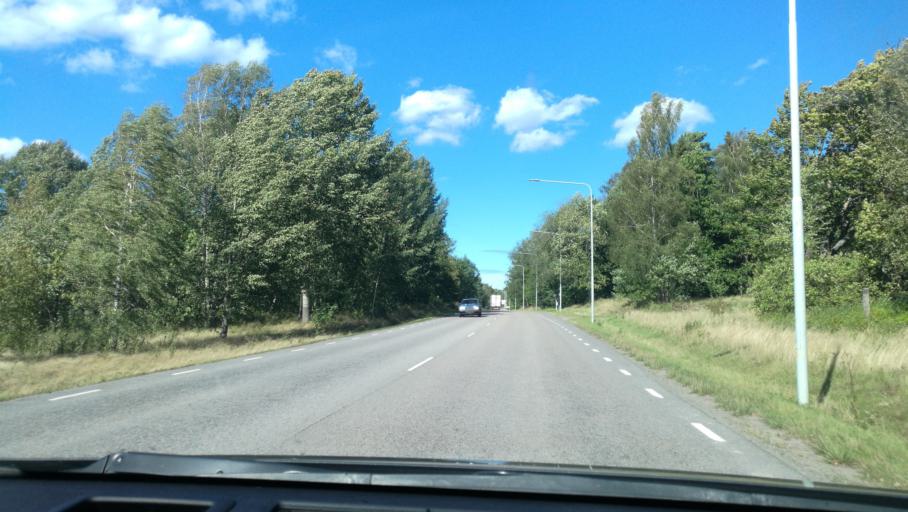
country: SE
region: Vaestra Goetaland
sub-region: Mariestads Kommun
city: Mariestad
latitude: 58.6866
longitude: 13.8442
